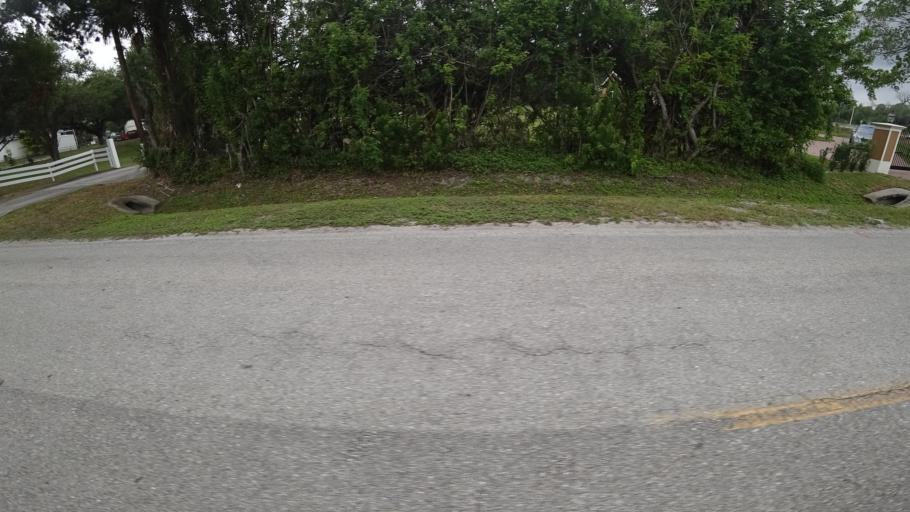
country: US
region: Florida
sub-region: Manatee County
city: Samoset
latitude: 27.4601
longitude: -82.5162
